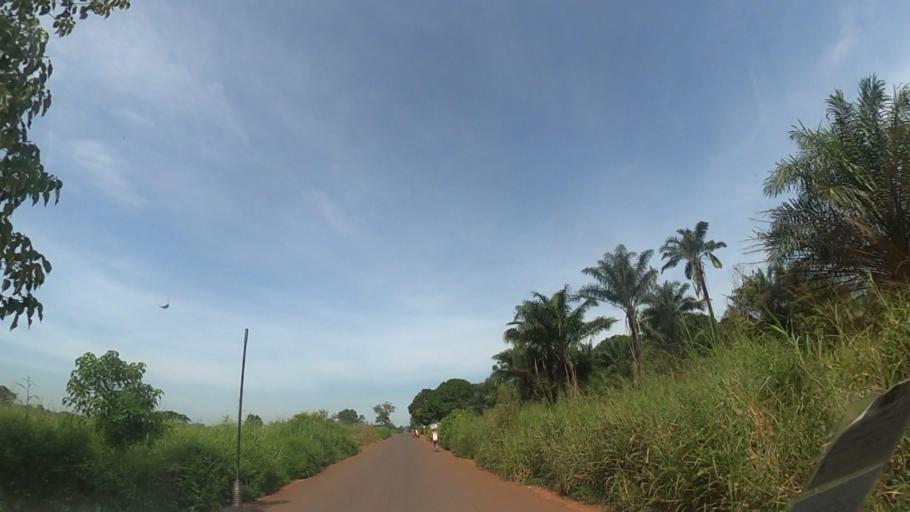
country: CF
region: Ombella-Mpoko
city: Bimbo
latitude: 4.3138
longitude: 18.4721
